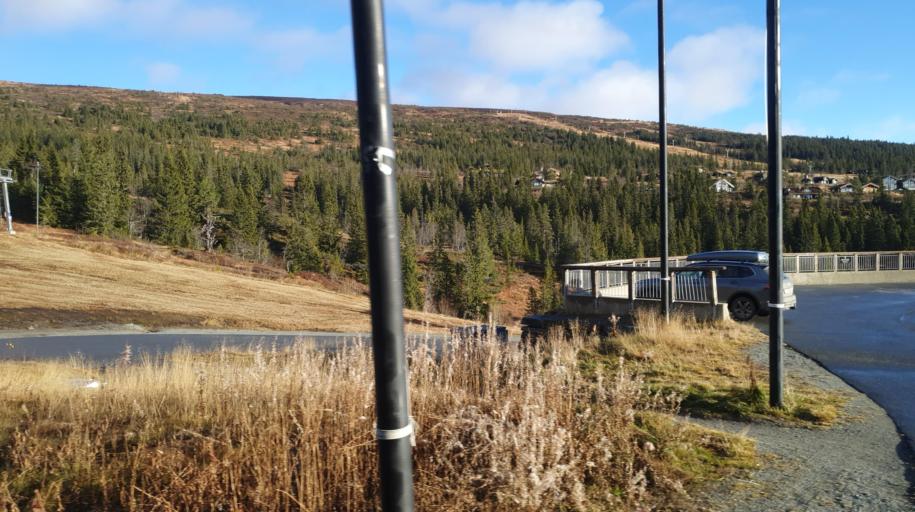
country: NO
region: Buskerud
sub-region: Krodsherad
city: Noresund
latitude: 60.2275
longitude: 9.5197
